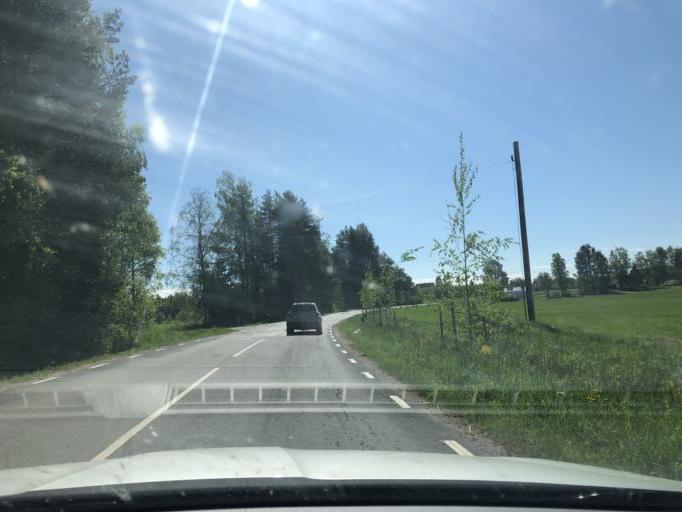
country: SE
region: Norrbotten
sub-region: Lulea Kommun
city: Gammelstad
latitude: 65.6550
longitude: 22.0145
